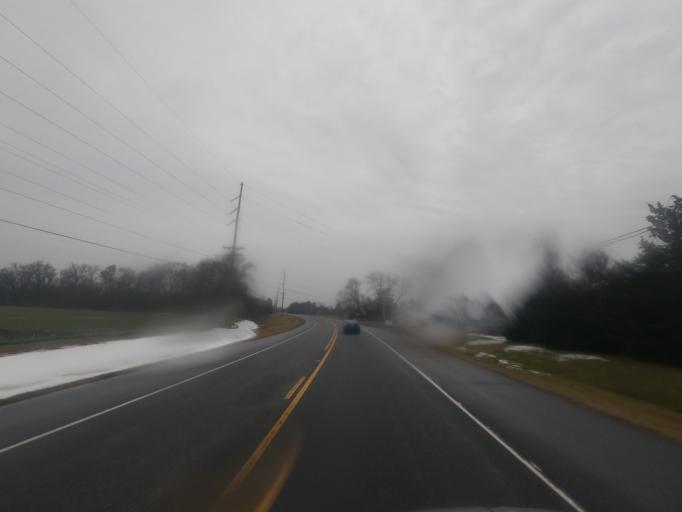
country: US
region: Maryland
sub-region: Dorchester County
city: Hurlock
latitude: 38.5826
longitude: -75.9632
